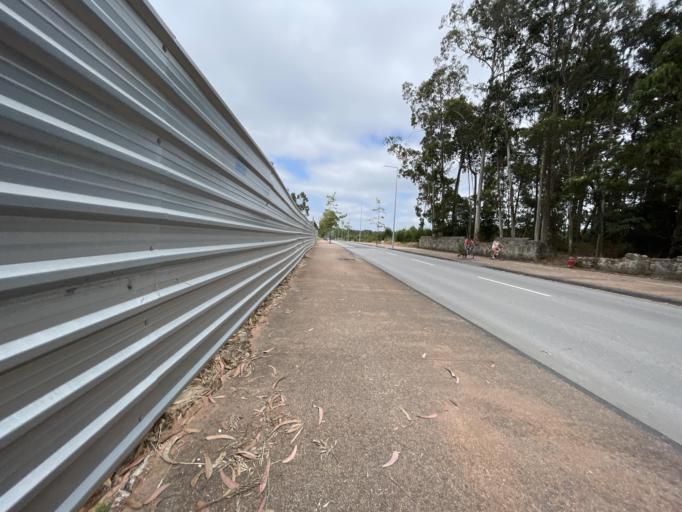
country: PT
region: Aveiro
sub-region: Ovar
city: Esmoriz
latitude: 40.9415
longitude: -8.6439
